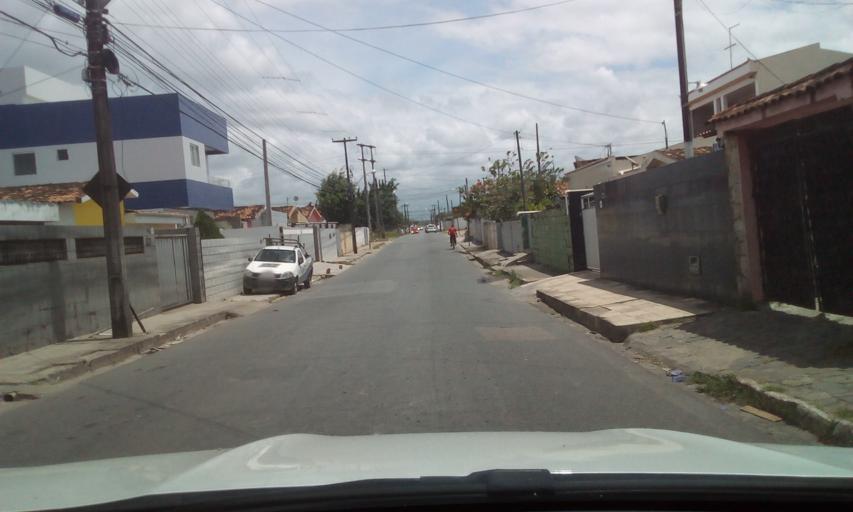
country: BR
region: Paraiba
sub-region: Bayeux
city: Bayeux
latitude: -7.1774
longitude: -34.8950
